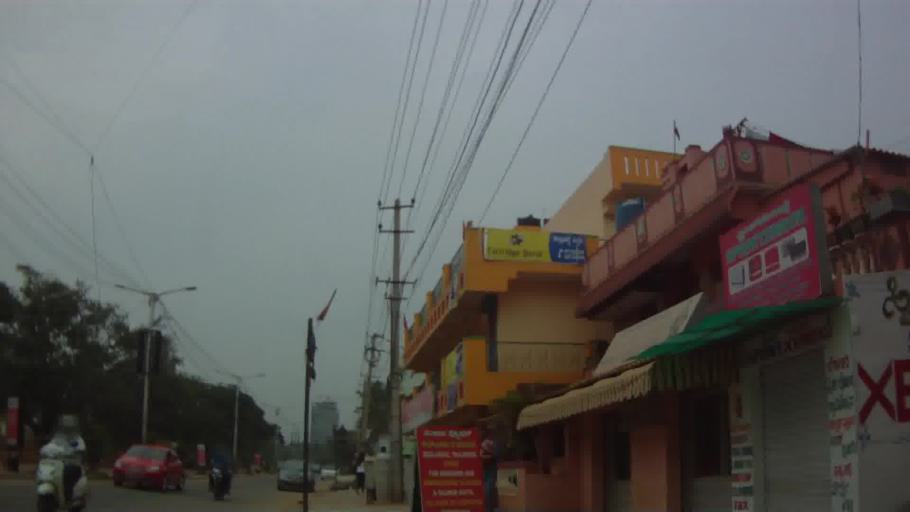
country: IN
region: Karnataka
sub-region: Bangalore Rural
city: Hoskote
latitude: 12.9569
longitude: 77.7386
